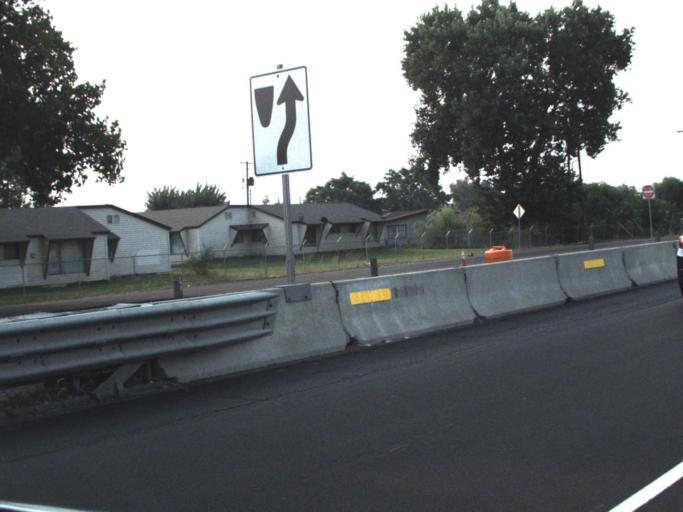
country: US
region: Washington
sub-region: Yakima County
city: Wapato
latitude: 46.4464
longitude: -120.4303
